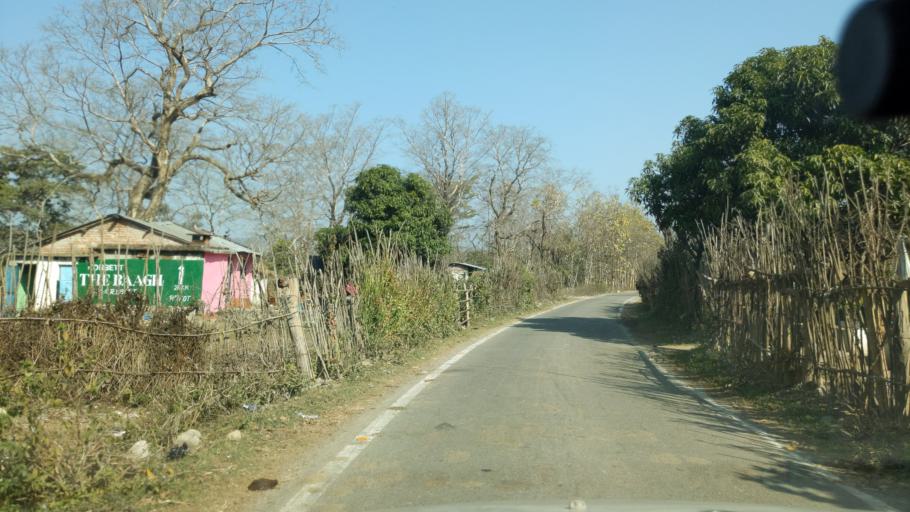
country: IN
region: Uttarakhand
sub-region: Naini Tal
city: Ramnagar
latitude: 29.4226
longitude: 79.1386
